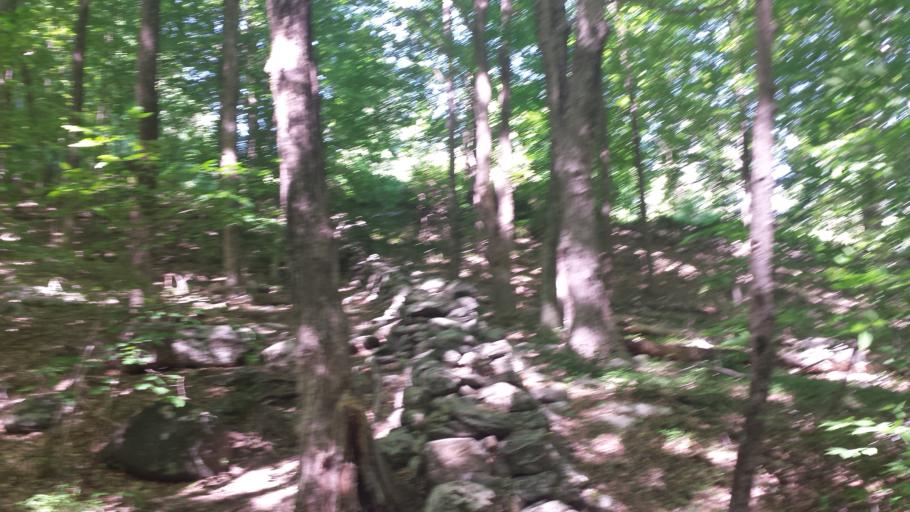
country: US
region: New York
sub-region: Westchester County
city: Pound Ridge
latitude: 41.2562
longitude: -73.5890
